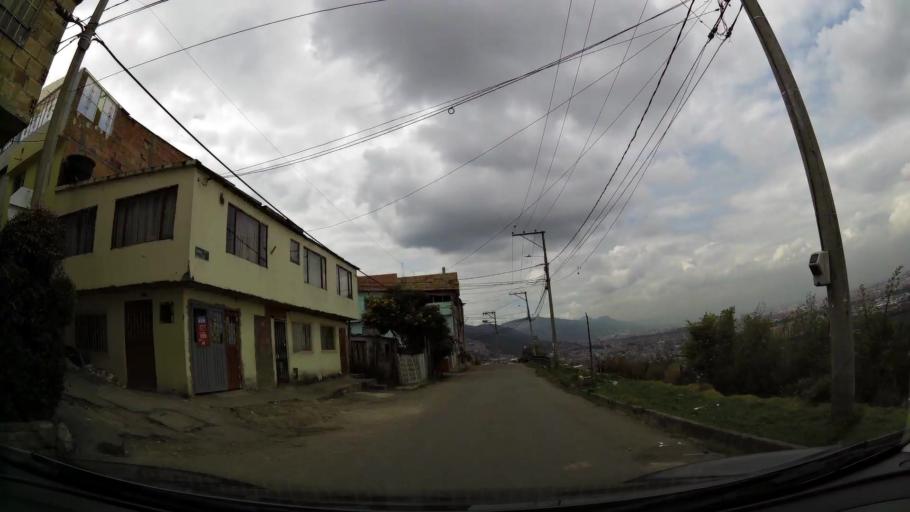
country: CO
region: Cundinamarca
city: La Calera
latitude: 4.7623
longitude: -74.0218
